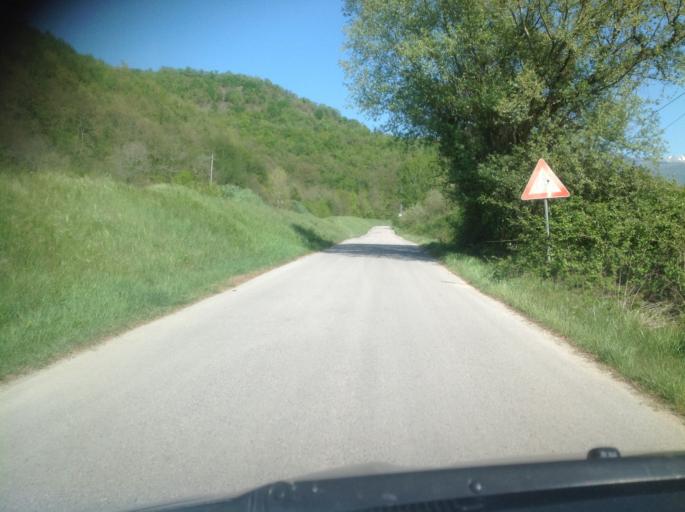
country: IT
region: Latium
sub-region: Provincia di Rieti
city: Colli sul Velino
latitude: 42.4937
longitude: 12.7845
